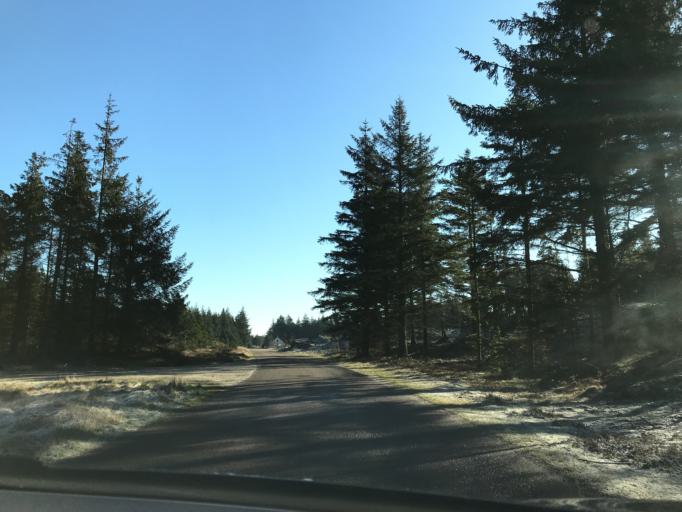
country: DK
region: South Denmark
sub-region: Varde Kommune
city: Oksbol
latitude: 55.7944
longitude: 8.2169
